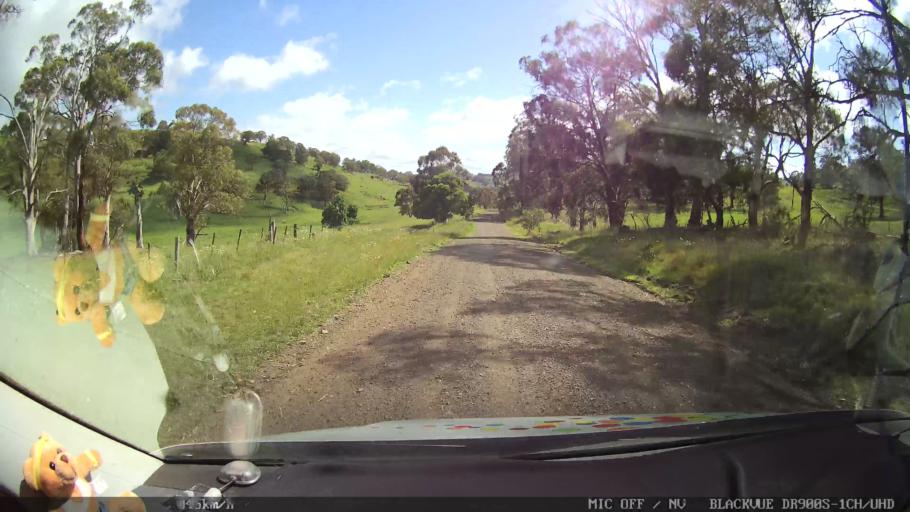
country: AU
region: New South Wales
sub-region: Guyra
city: Guyra
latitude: -29.9889
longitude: 151.6892
